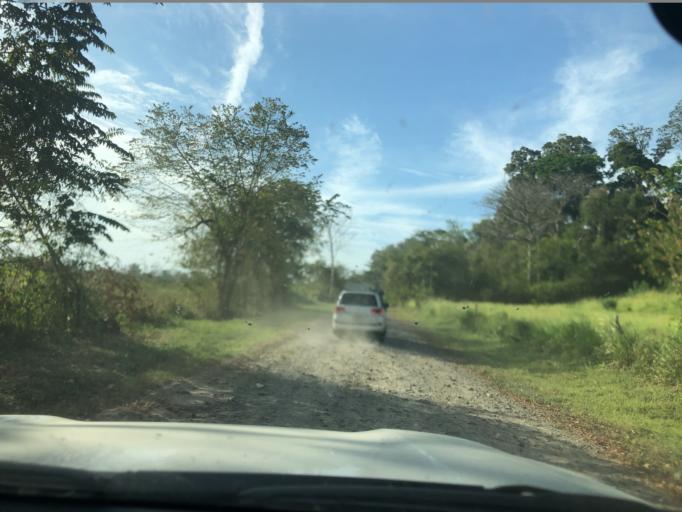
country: CR
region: Alajuela
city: San Jose
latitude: 11.1193
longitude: -85.2855
